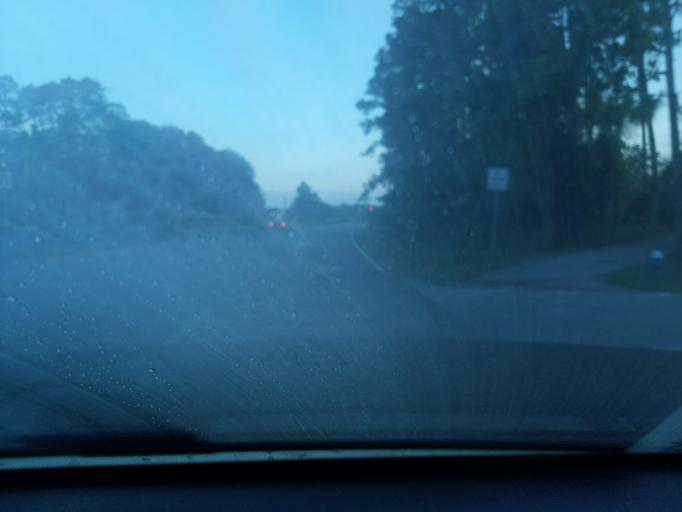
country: US
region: Florida
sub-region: Flagler County
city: Palm Coast
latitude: 29.5470
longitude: -81.2342
